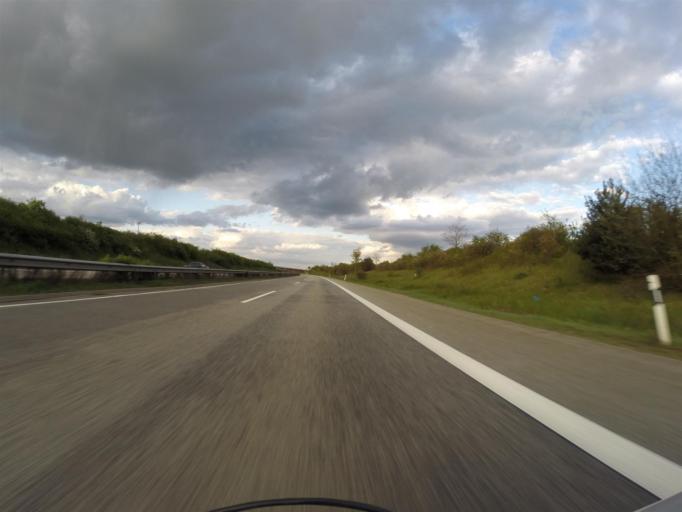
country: DE
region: Rheinland-Pfalz
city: Borrstadt
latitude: 49.5821
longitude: 7.9337
